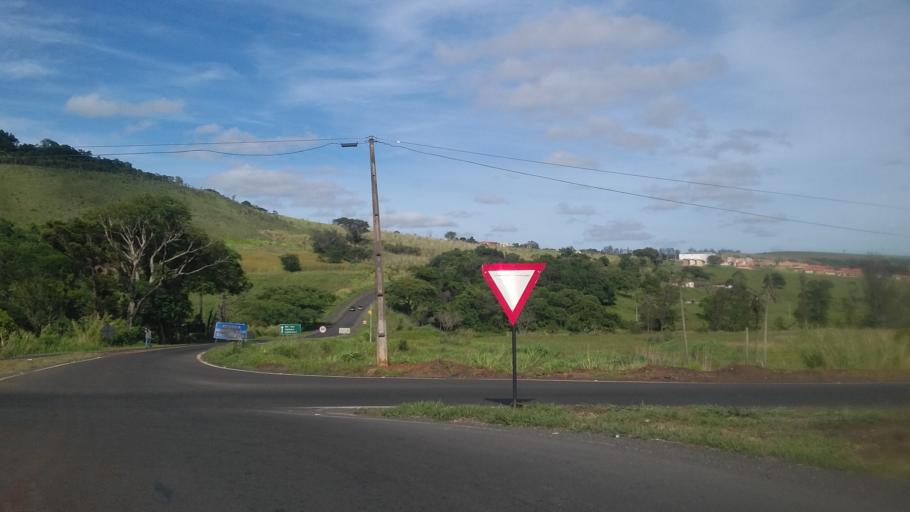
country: BR
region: Parana
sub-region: Santo Antonio Da Platina
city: Santo Antonio da Platina
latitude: -23.2795
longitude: -50.0558
